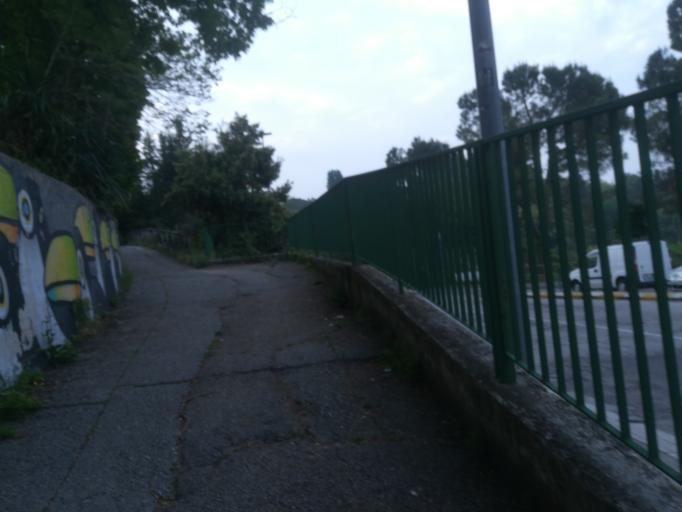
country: IT
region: The Marches
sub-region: Provincia di Macerata
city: Macerata
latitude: 43.2990
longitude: 13.4464
